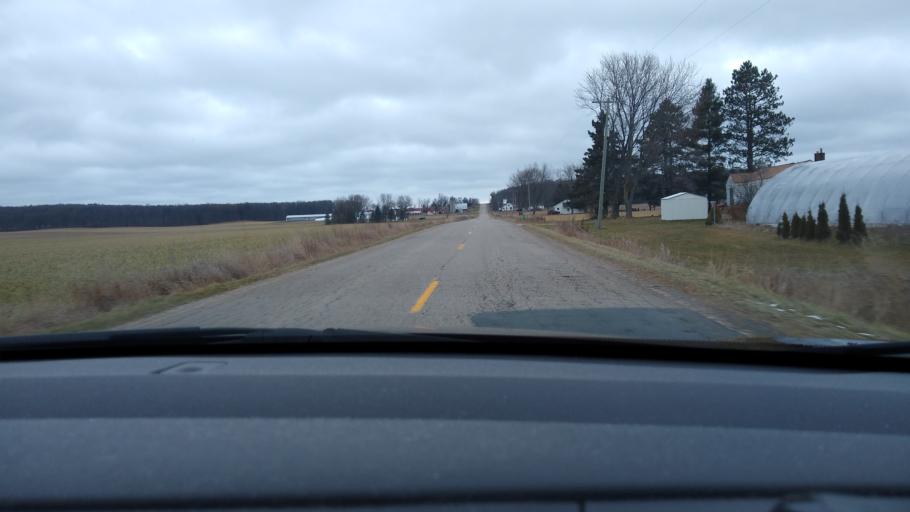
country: US
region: Michigan
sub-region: Missaukee County
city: Lake City
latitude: 44.2801
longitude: -85.0541
